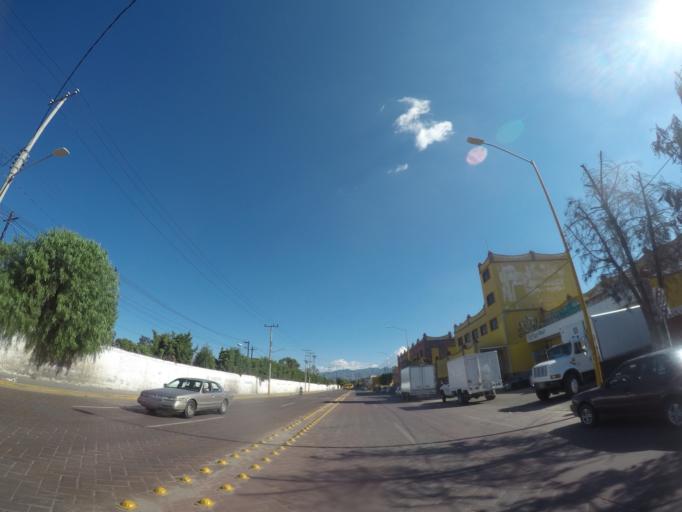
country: MX
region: San Luis Potosi
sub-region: San Luis Potosi
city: San Luis Potosi
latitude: 22.1598
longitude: -100.9719
